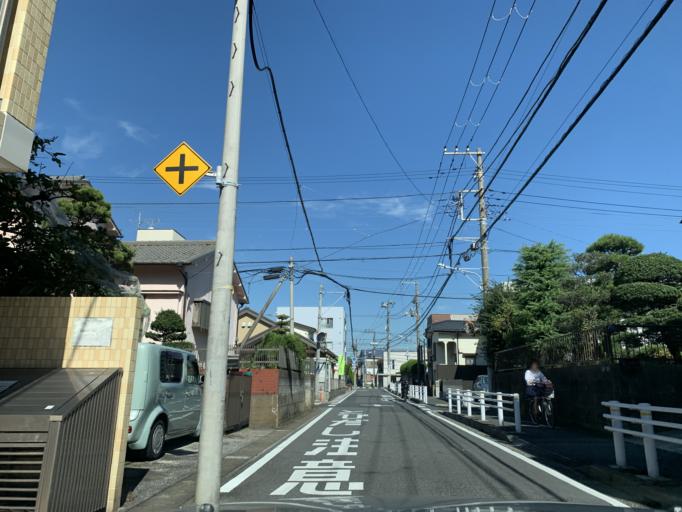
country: JP
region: Tokyo
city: Urayasu
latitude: 35.6558
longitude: 139.8916
